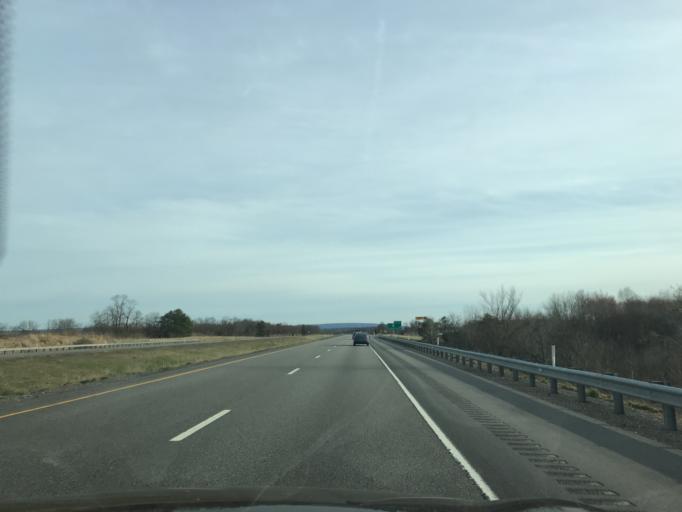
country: US
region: Pennsylvania
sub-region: Northumberland County
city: Watsontown
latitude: 41.1276
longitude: -76.8008
